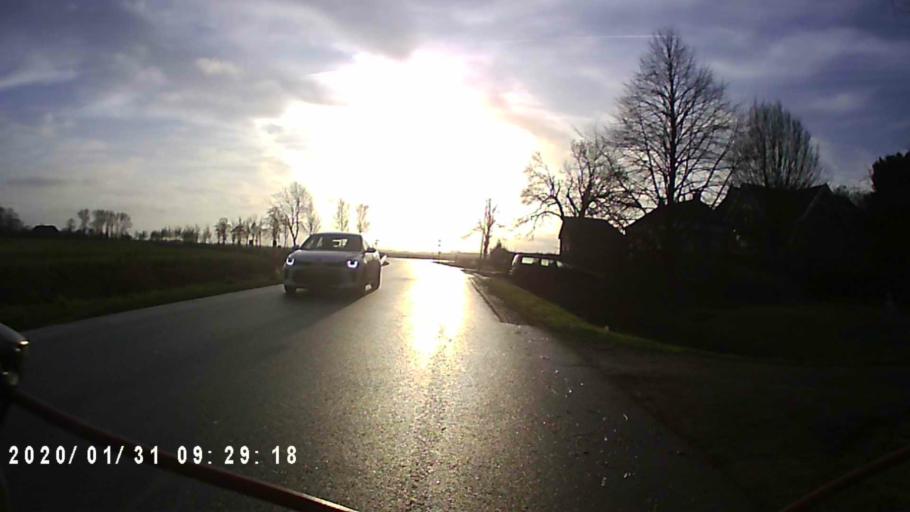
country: NL
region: Groningen
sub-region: Gemeente Zuidhorn
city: Aduard
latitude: 53.3053
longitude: 6.4479
